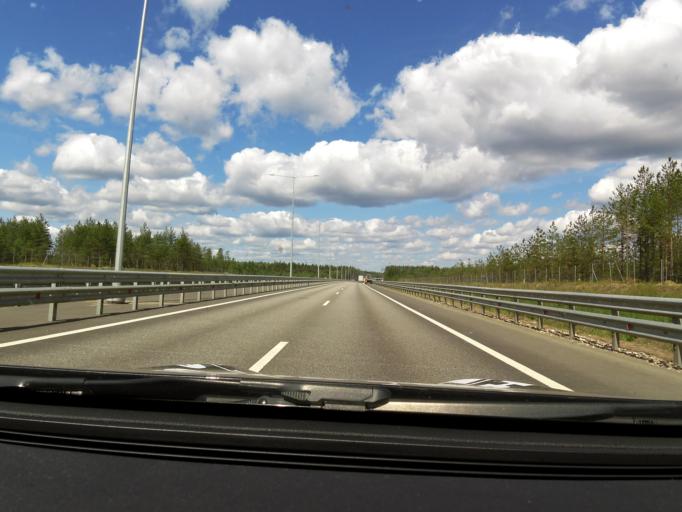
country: RU
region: Tverskaya
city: Krasnomayskiy
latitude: 57.4904
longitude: 34.3107
